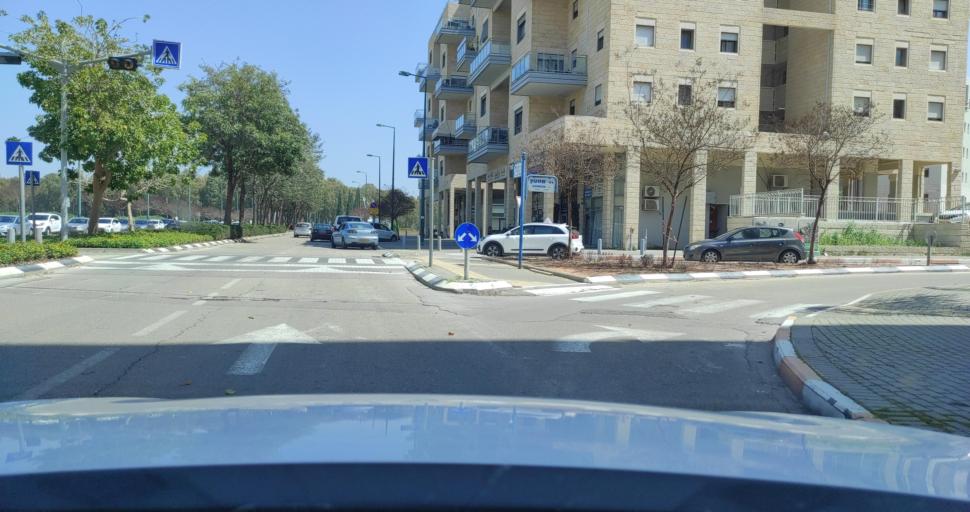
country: IL
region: Central District
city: Nordiyya
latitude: 32.3029
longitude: 34.8714
